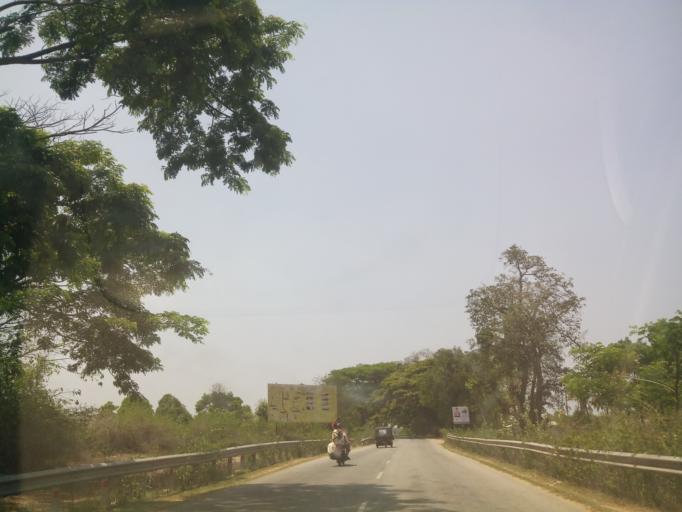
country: IN
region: Karnataka
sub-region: Hassan
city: Alur
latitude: 12.9520
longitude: 75.9724
